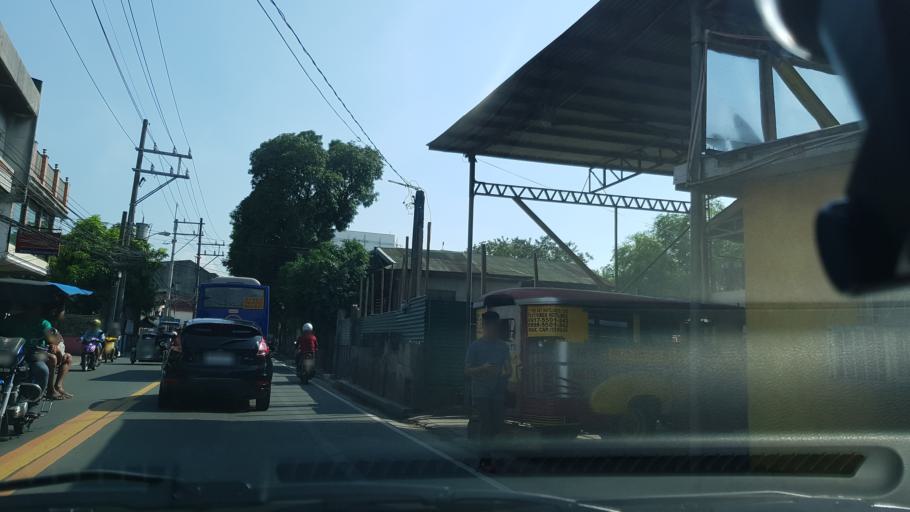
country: PH
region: Metro Manila
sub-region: Marikina
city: Calumpang
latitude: 14.6397
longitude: 121.0942
